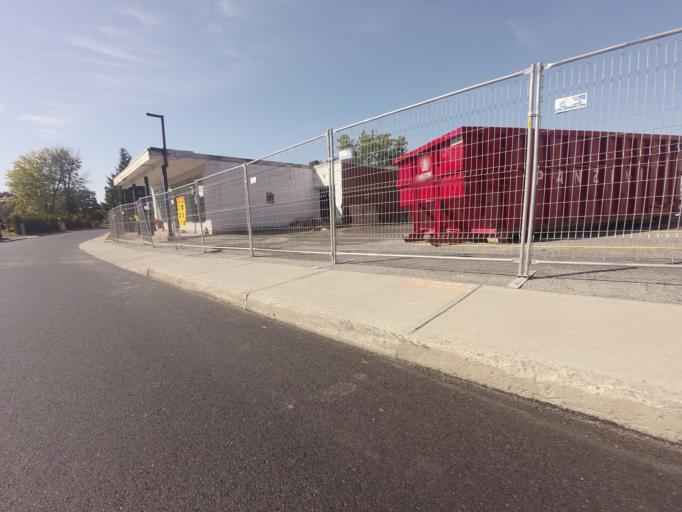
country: CA
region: Quebec
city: Kirkland
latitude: 45.4816
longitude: -73.8698
